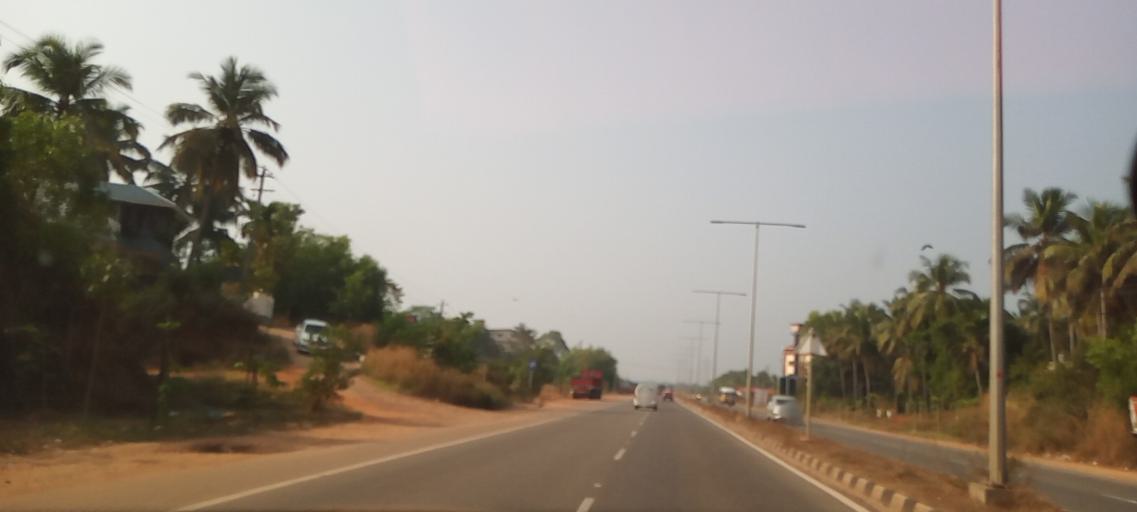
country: IN
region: Karnataka
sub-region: Udupi
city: Coondapoor
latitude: 13.6533
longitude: 74.7077
